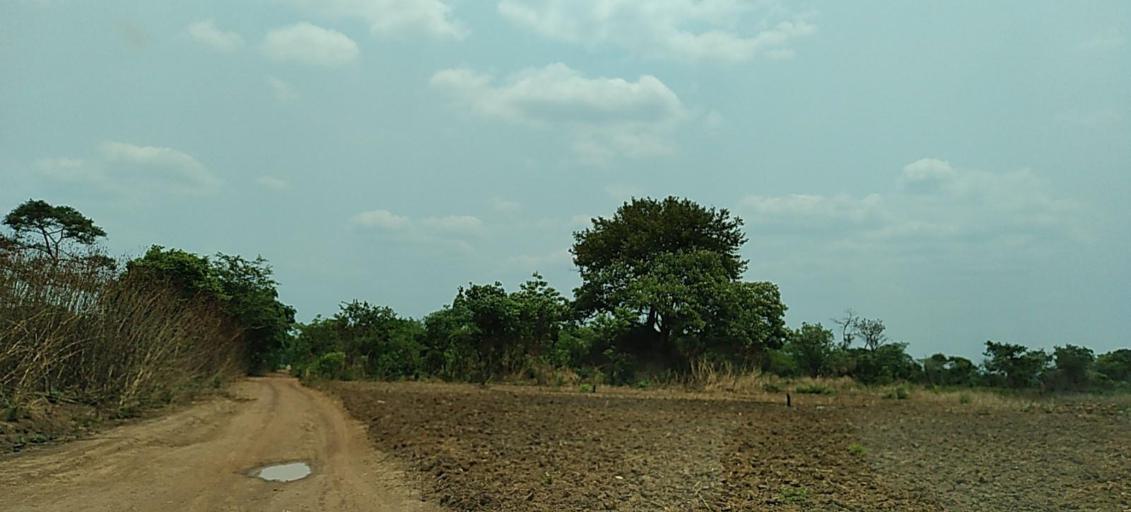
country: ZM
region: Copperbelt
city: Kalulushi
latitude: -12.7988
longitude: 28.0060
